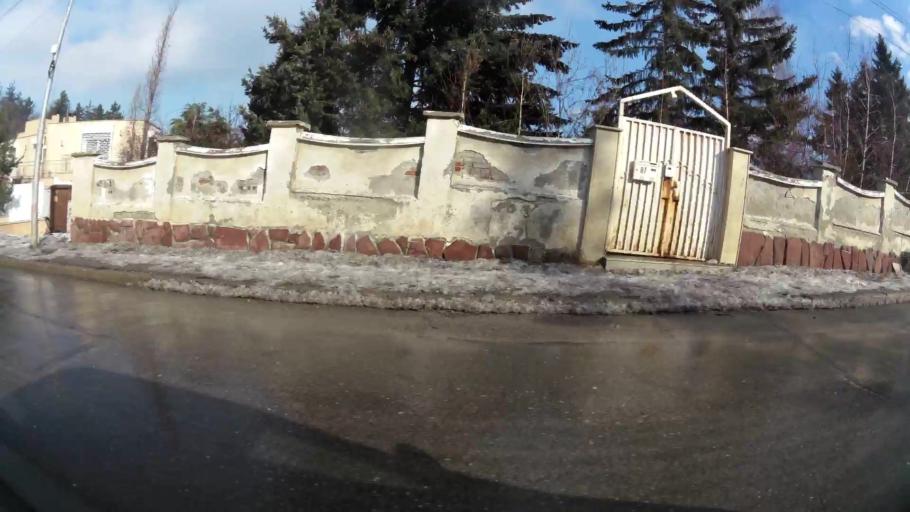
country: BG
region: Sofia-Capital
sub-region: Stolichna Obshtina
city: Sofia
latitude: 42.6480
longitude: 23.2451
